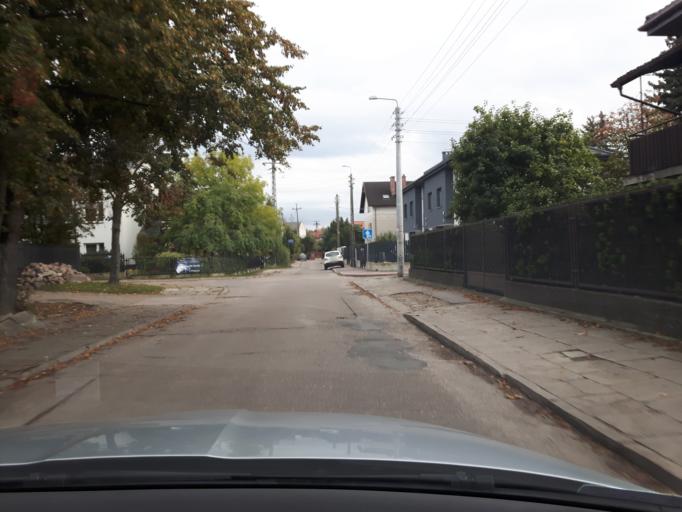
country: PL
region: Masovian Voivodeship
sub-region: Powiat wolominski
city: Zabki
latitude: 52.2892
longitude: 21.1236
